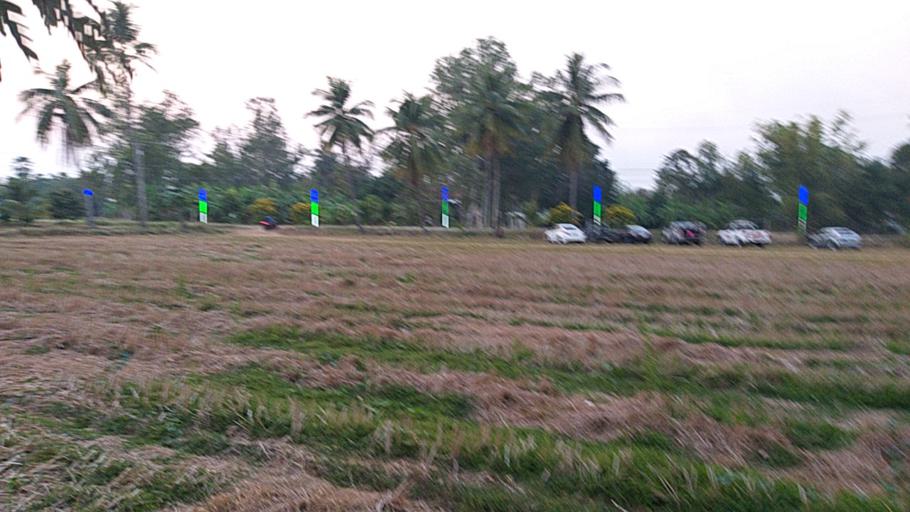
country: TH
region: Sing Buri
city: Sing Buri
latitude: 14.8352
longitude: 100.4018
